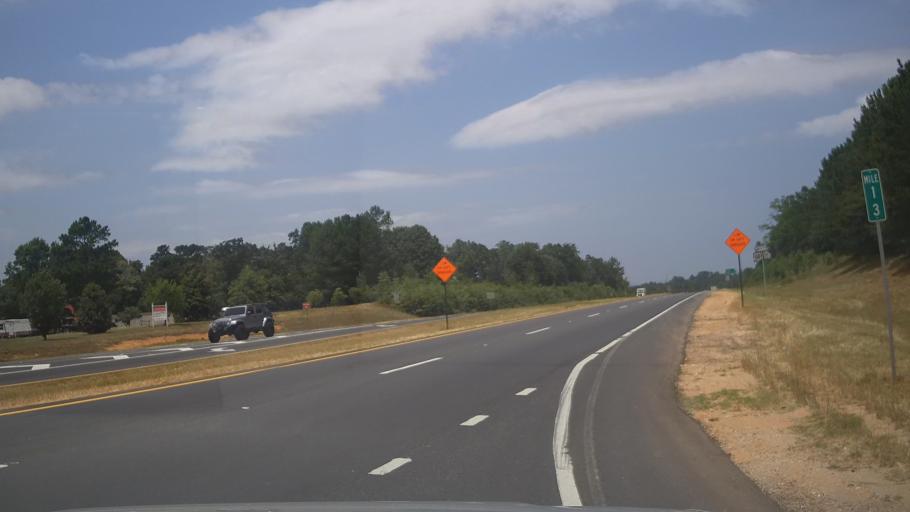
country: US
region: Georgia
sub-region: Jackson County
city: Commerce
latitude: 34.1938
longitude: -83.4314
